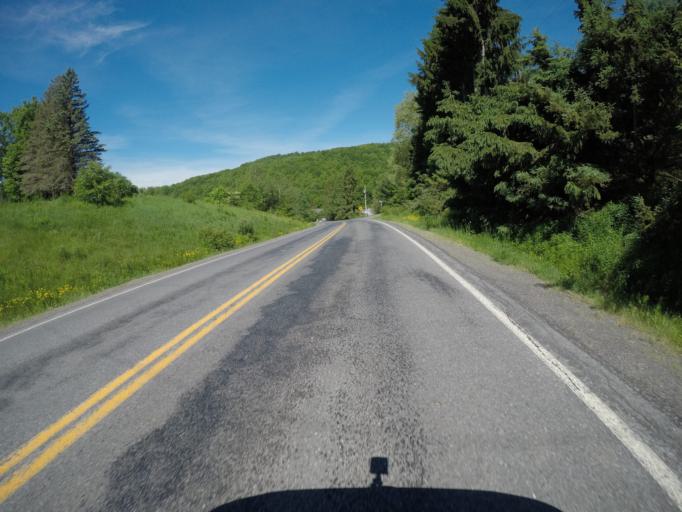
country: US
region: New York
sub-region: Delaware County
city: Delhi
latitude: 42.2157
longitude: -74.9036
